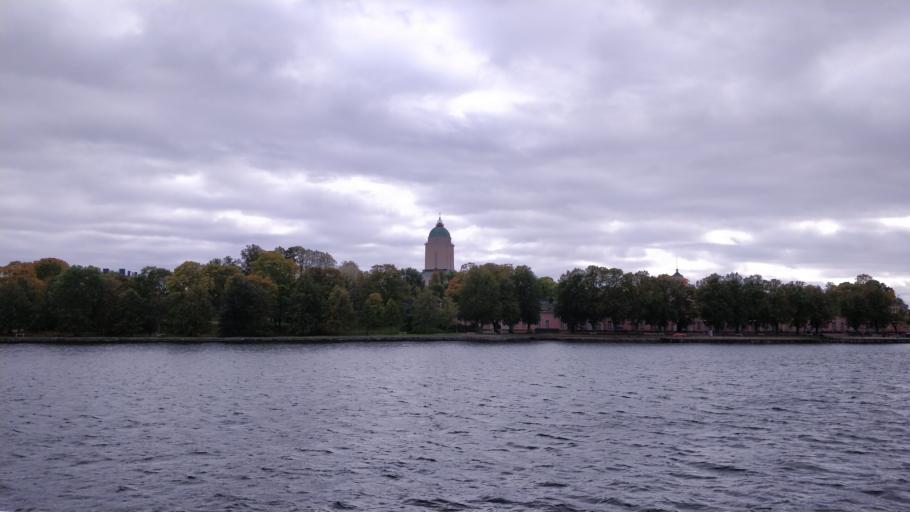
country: FI
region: Uusimaa
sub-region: Helsinki
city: Helsinki
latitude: 60.1510
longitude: 24.9873
